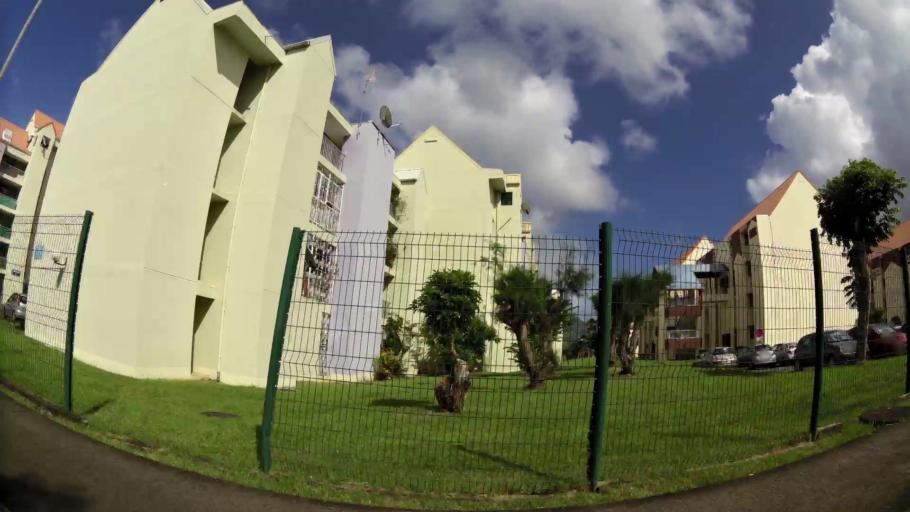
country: MQ
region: Martinique
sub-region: Martinique
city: Le Lamentin
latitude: 14.6166
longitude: -60.9879
